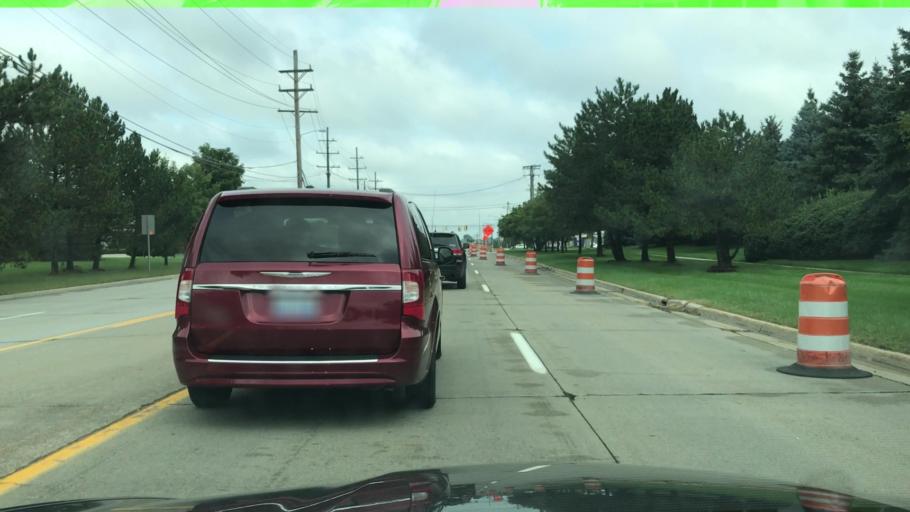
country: US
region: Michigan
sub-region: Macomb County
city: Sterling Heights
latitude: 42.5796
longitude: -83.0529
